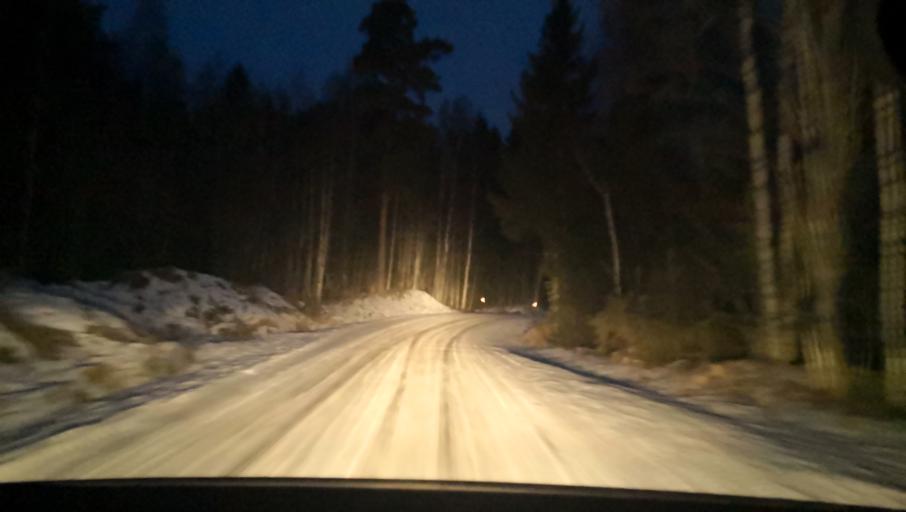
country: SE
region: Uppsala
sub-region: Heby Kommun
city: Tarnsjo
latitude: 60.2606
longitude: 16.7808
